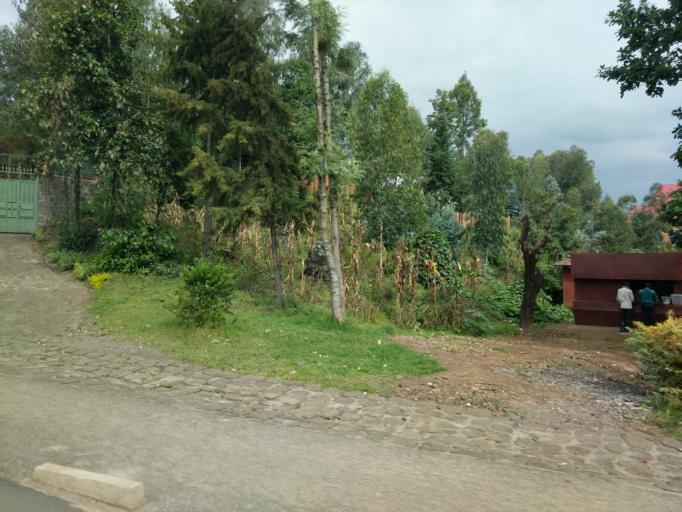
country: RW
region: Northern Province
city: Musanze
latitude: -1.5001
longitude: 29.6230
